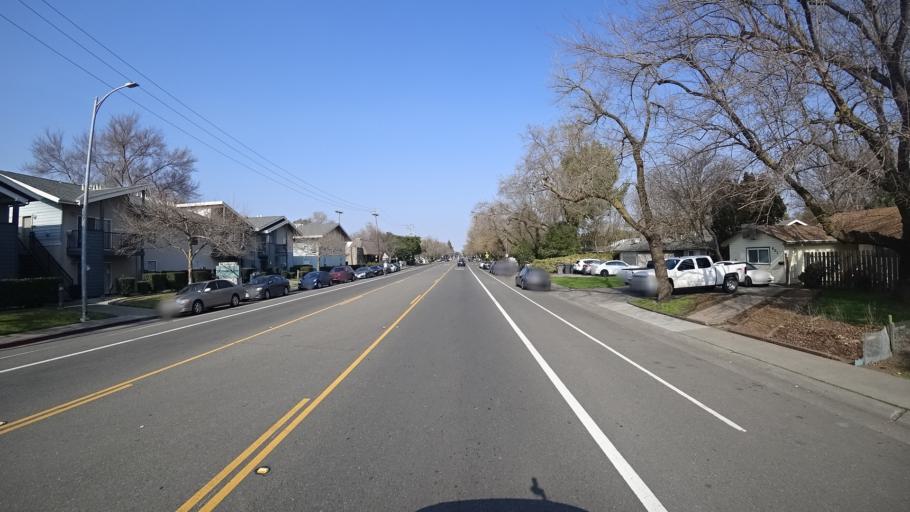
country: US
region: California
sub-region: Yolo County
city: Davis
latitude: 38.5478
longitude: -121.7587
